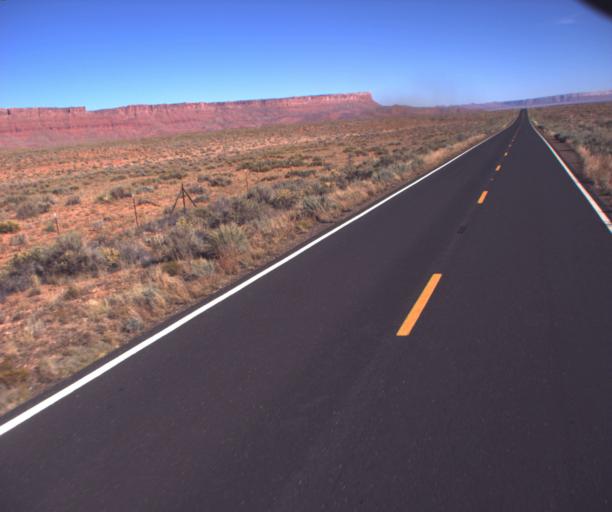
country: US
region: Arizona
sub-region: Coconino County
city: Page
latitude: 36.7154
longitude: -111.9924
